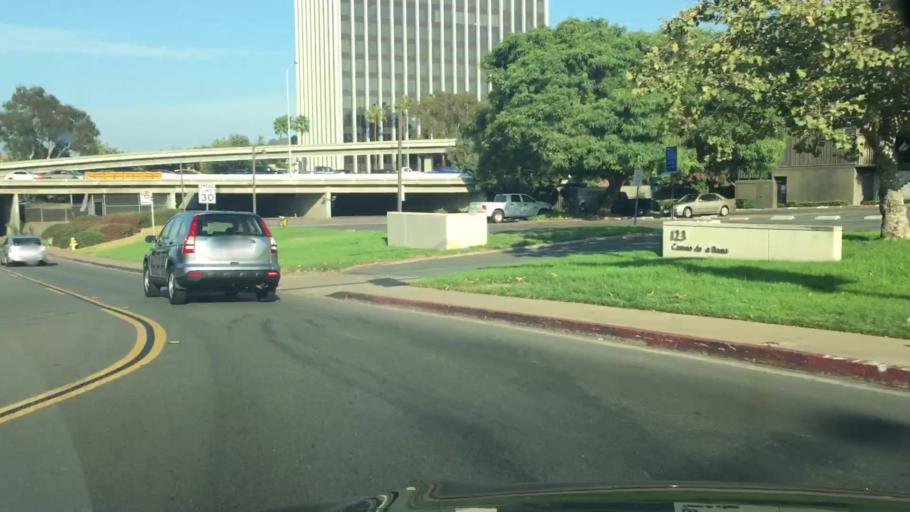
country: US
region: California
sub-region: San Diego County
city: San Diego
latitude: 32.7659
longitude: -117.1640
